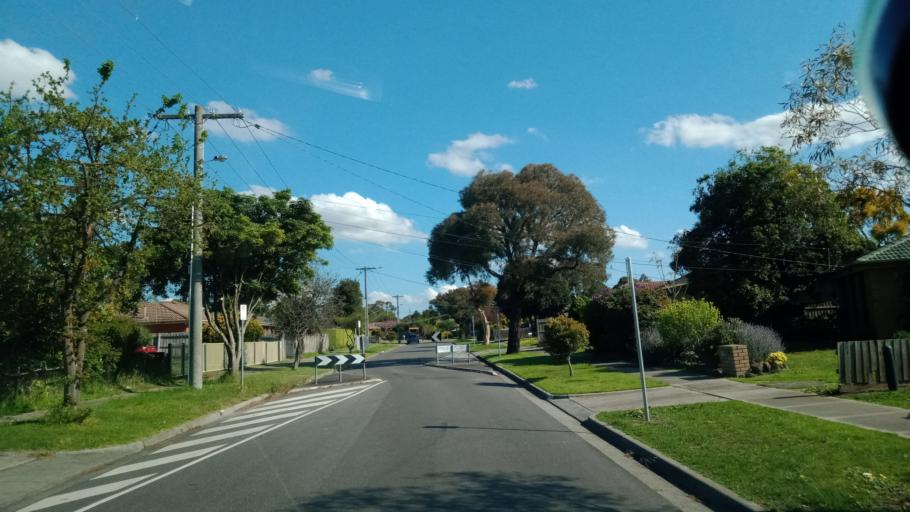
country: AU
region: Victoria
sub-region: Casey
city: Cranbourne West
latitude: -38.1058
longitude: 145.2713
